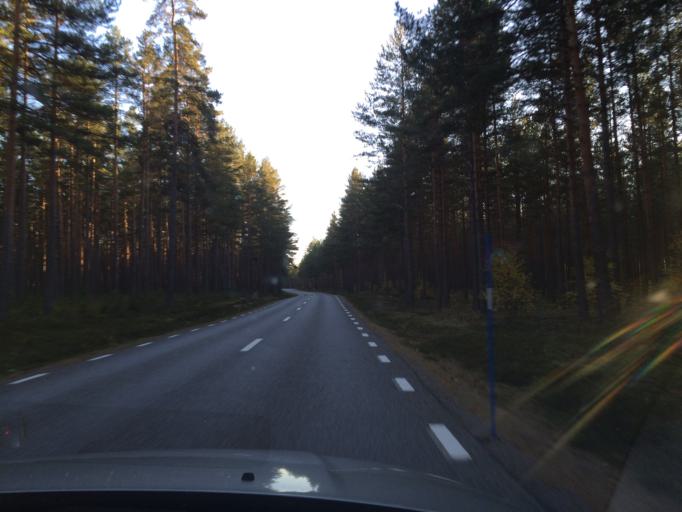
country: SE
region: Gaevleborg
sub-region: Sandvikens Kommun
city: Arsunda
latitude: 60.4984
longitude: 16.7255
